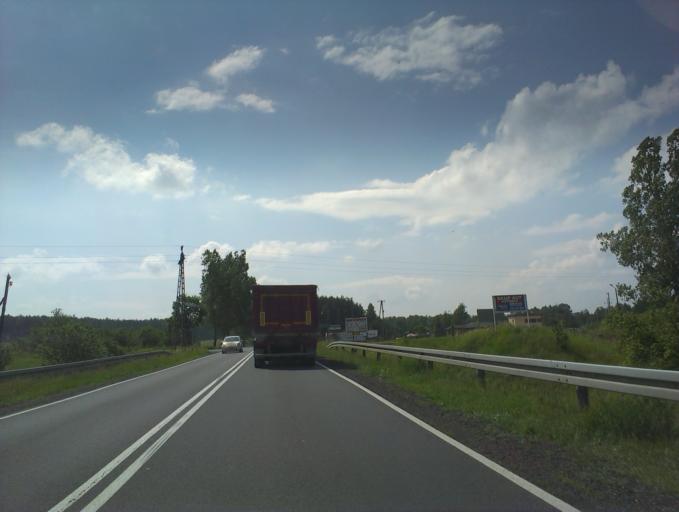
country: PL
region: Greater Poland Voivodeship
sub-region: Powiat zlotowski
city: Tarnowka
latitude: 53.2629
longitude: 16.7820
